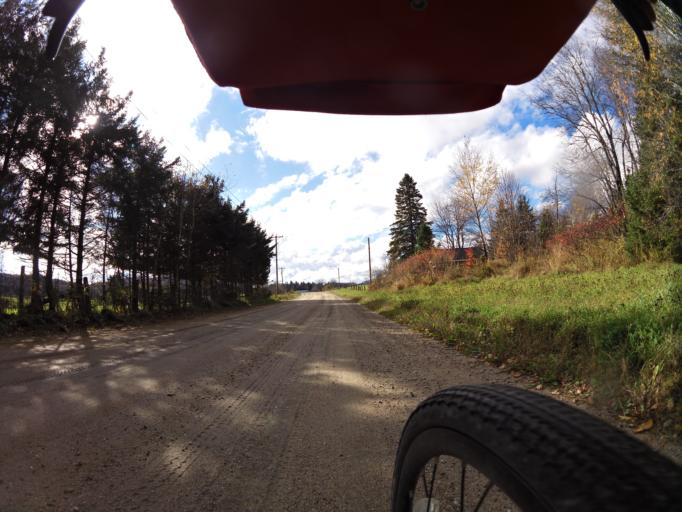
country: CA
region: Quebec
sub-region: Outaouais
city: Wakefield
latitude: 45.6974
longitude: -76.0666
